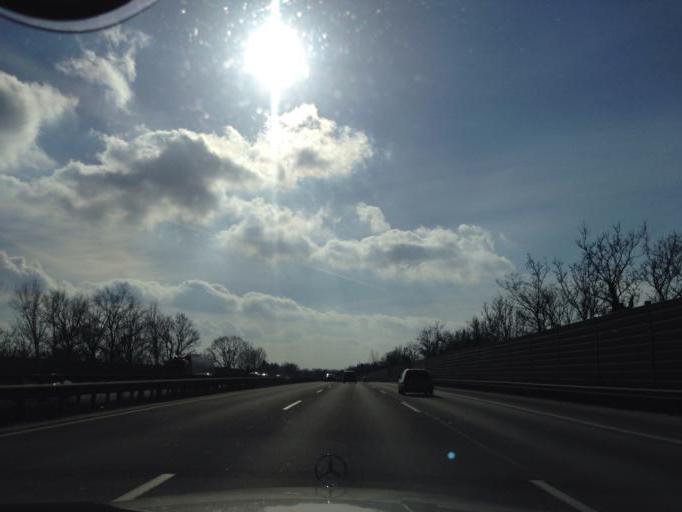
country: DE
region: Hamburg
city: Harburg
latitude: 53.4219
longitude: 10.0325
